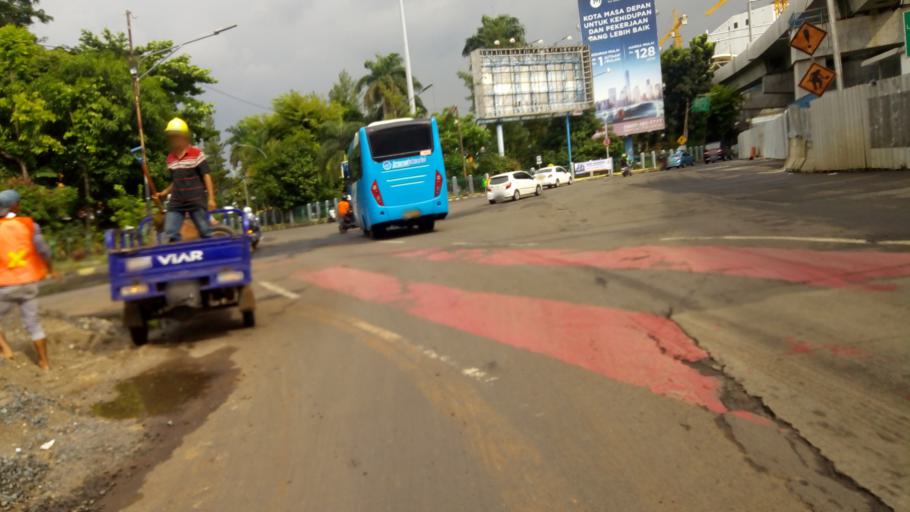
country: ID
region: Jakarta Raya
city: Jakarta
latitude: -6.2422
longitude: 106.7986
